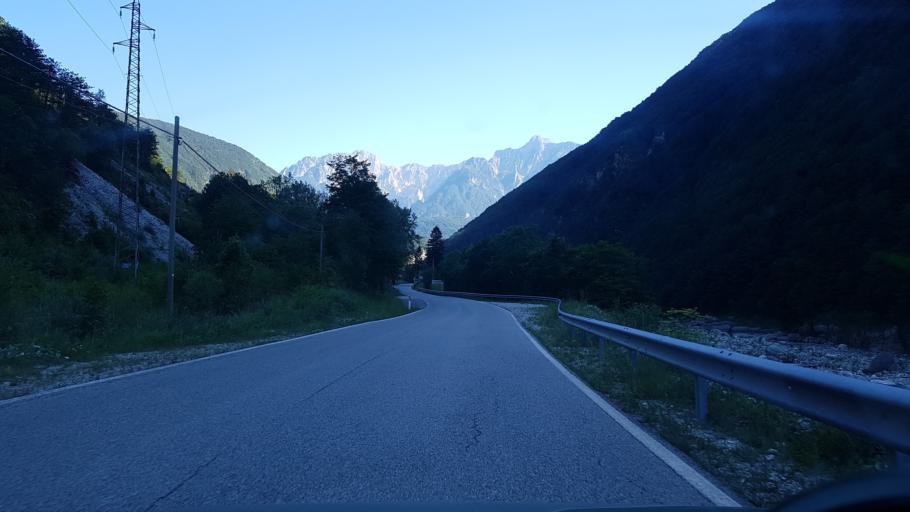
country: IT
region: Friuli Venezia Giulia
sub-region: Provincia di Udine
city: Moggio Udinese
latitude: 46.4365
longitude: 13.1983
